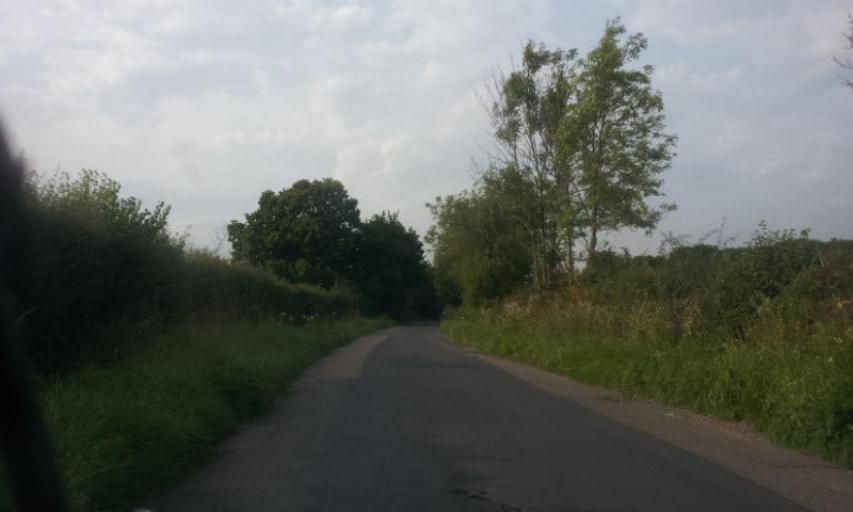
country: GB
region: England
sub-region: Kent
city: Yalding
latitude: 51.1957
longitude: 0.4155
